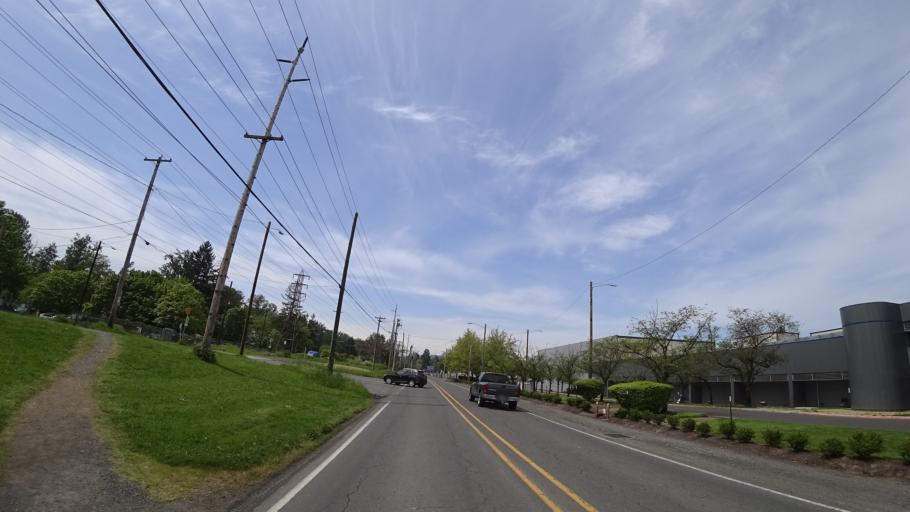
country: US
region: Oregon
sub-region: Clackamas County
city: Milwaukie
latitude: 45.4600
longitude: -122.6112
